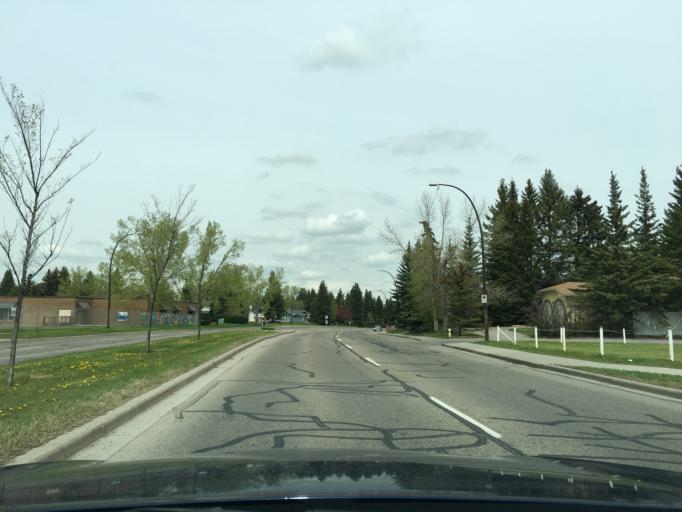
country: CA
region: Alberta
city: Calgary
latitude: 50.9428
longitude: -114.0858
